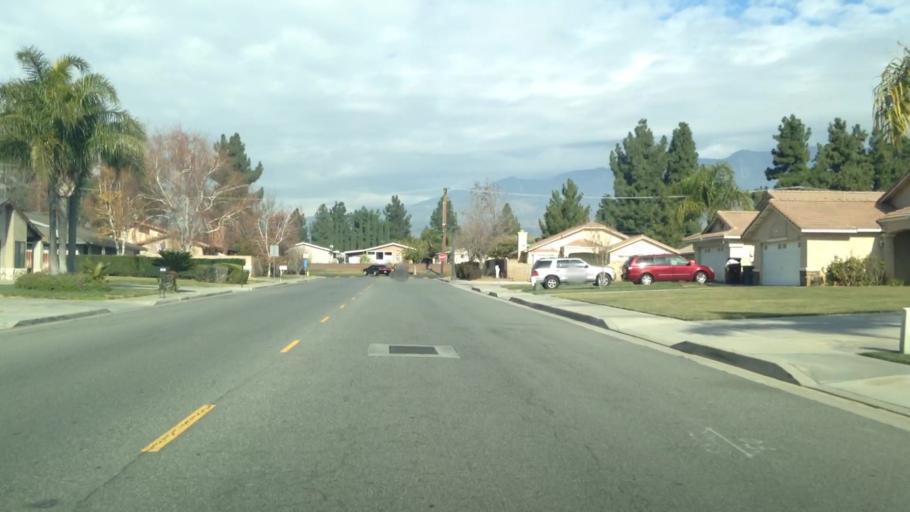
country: US
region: California
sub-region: Riverside County
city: Beaumont
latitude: 33.9458
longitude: -116.9661
